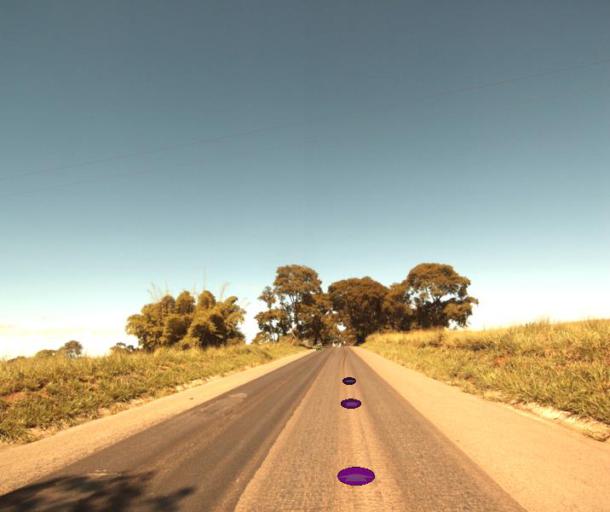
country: BR
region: Goias
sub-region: Itapaci
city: Itapaci
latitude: -15.1157
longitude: -49.4942
